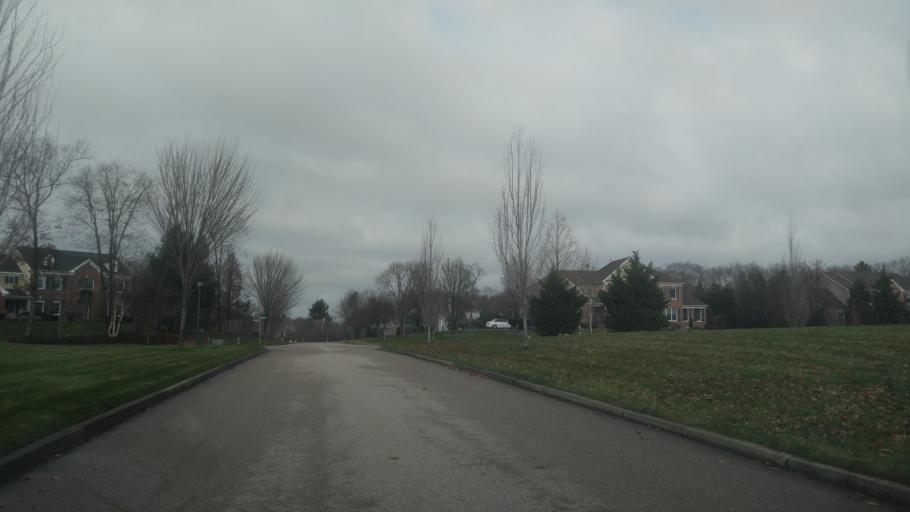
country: US
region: Rhode Island
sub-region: Washington County
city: Exeter
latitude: 41.6345
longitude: -71.5348
